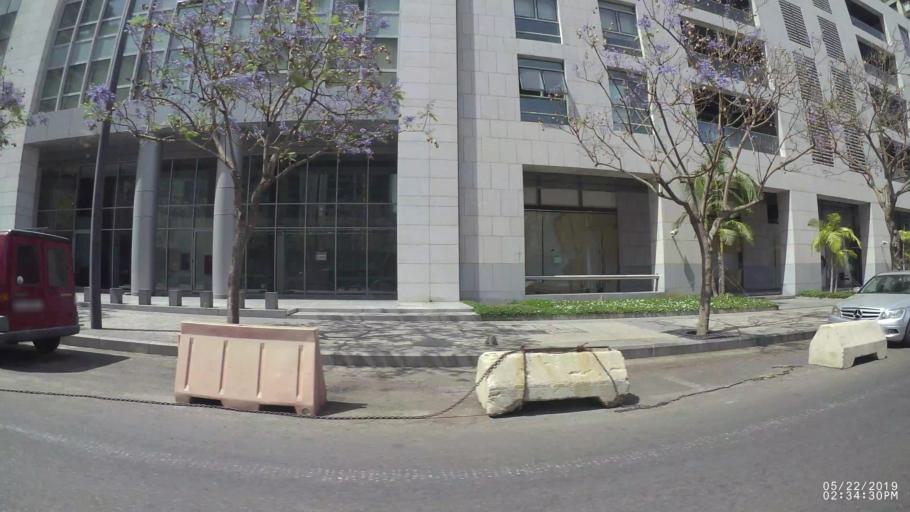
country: LB
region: Beyrouth
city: Beirut
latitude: 33.9003
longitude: 35.4975
